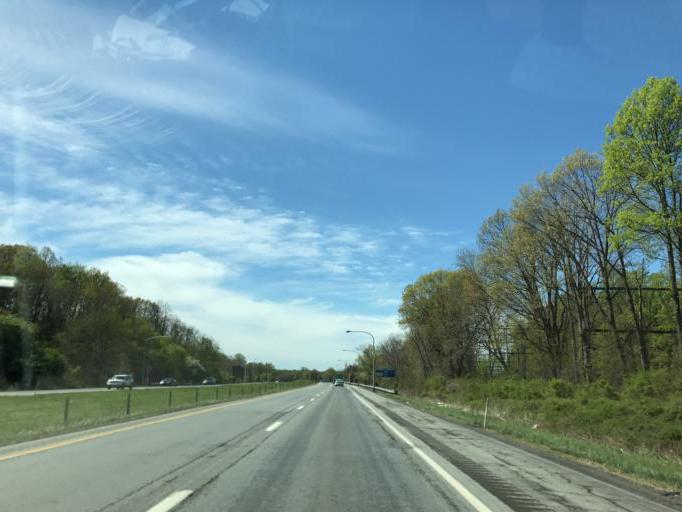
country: US
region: Pennsylvania
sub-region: Bucks County
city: Langhorne Manor
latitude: 40.1730
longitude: -74.8980
